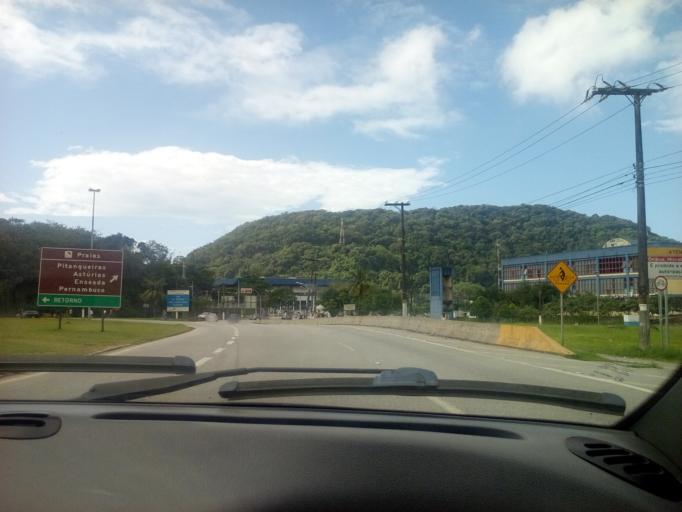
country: BR
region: Sao Paulo
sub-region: Guaruja
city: Guaruja
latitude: -23.9838
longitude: -46.2651
